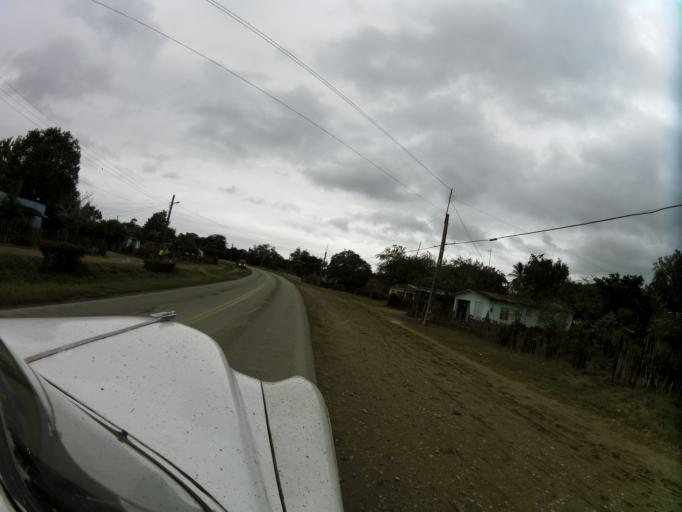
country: CU
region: Las Tunas
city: Las Tunas
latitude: 20.9222
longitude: -76.8697
